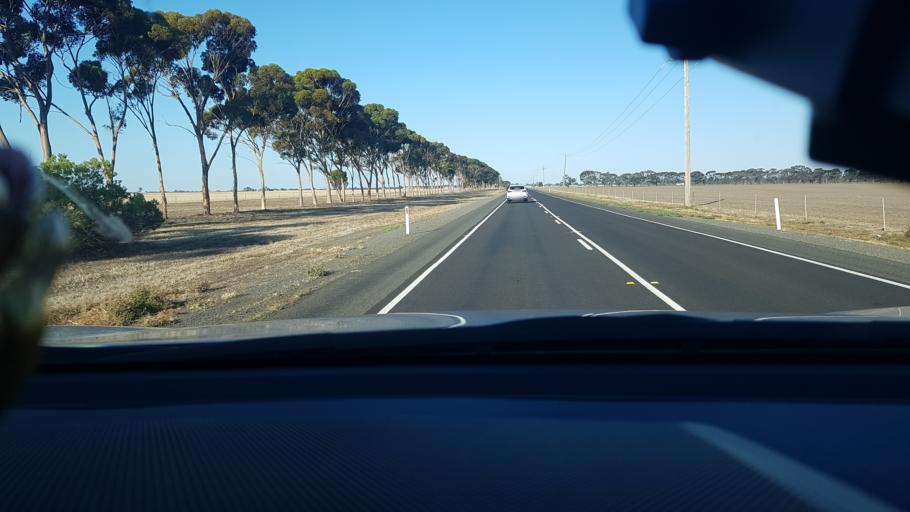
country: AU
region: Victoria
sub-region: Horsham
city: Horsham
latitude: -36.7313
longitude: 142.1436
